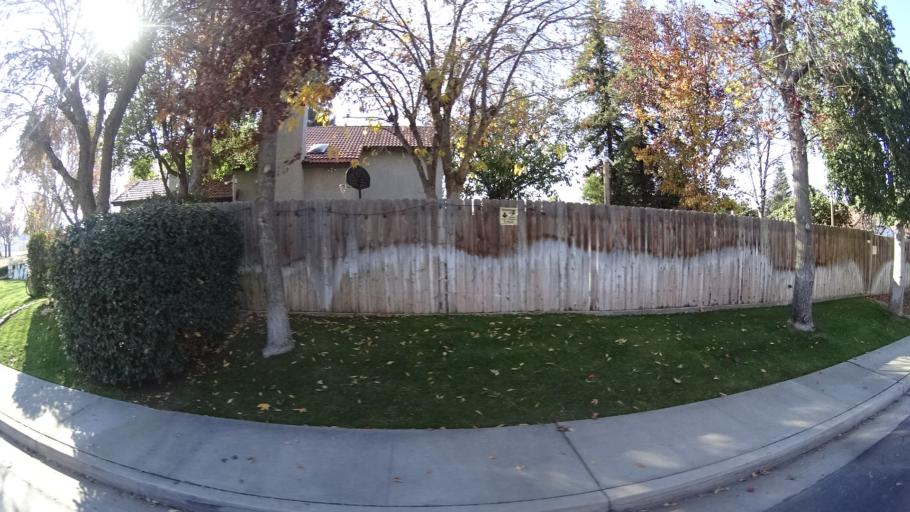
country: US
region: California
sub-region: Kern County
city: Greenacres
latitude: 35.3157
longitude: -119.1013
